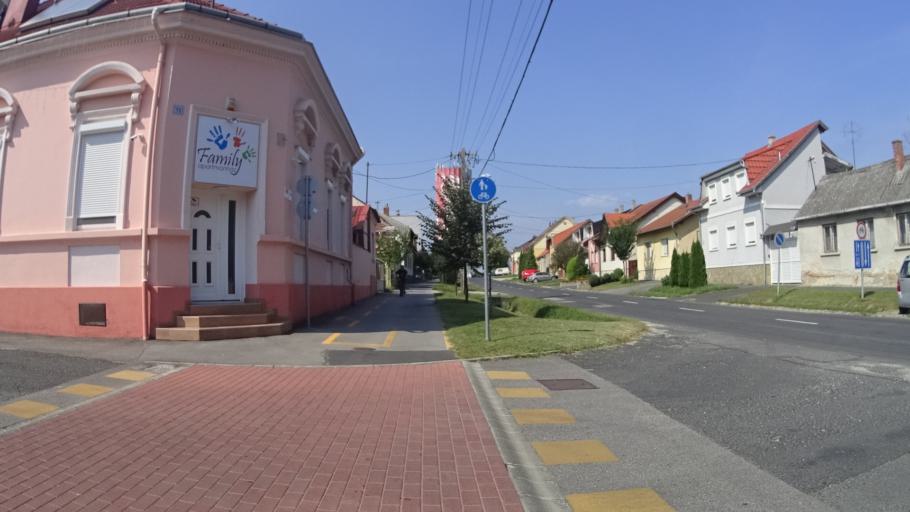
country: HU
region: Zala
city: Nagykanizsa
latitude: 46.4615
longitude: 16.9987
